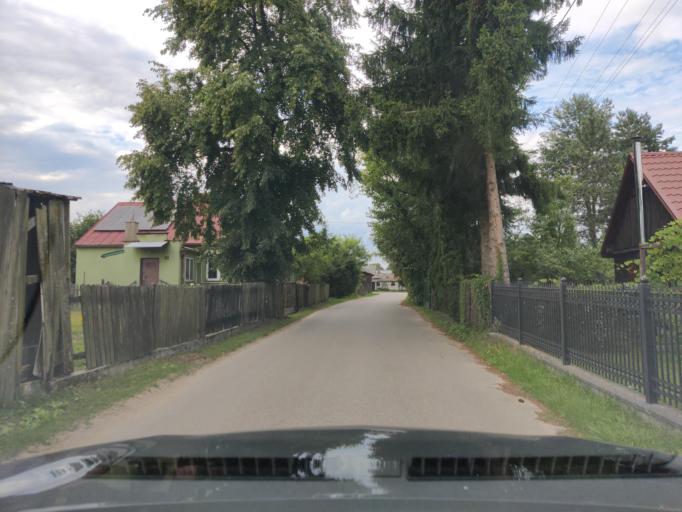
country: PL
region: Masovian Voivodeship
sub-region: Powiat pultuski
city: Pultusk
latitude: 52.7258
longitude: 21.1253
